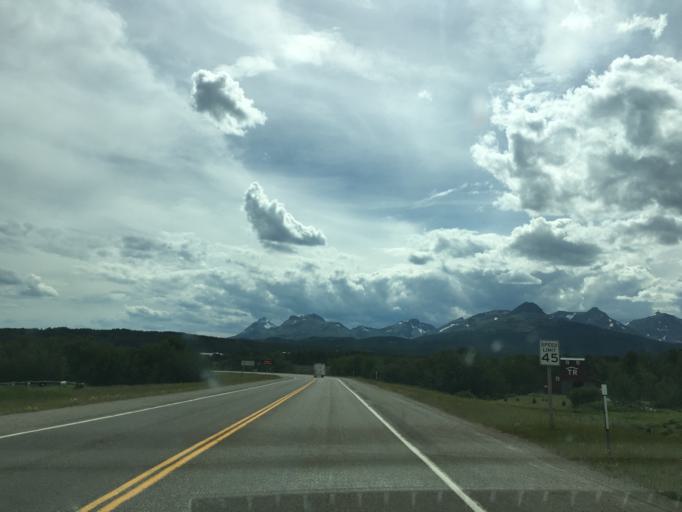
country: US
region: Montana
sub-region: Glacier County
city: South Browning
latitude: 48.4480
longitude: -113.2136
